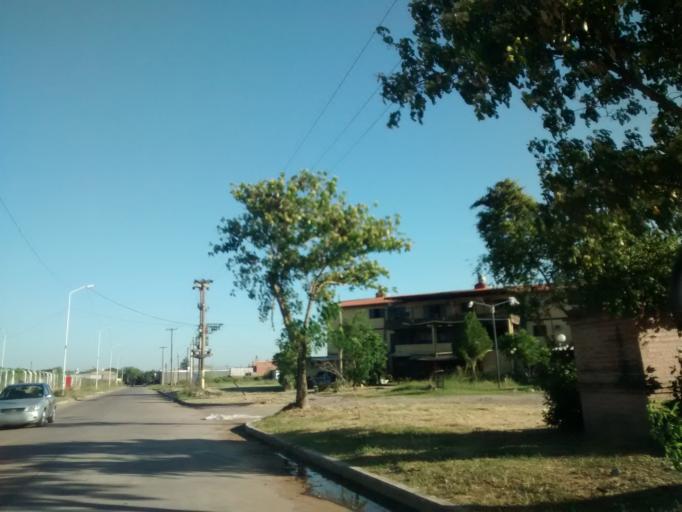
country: AR
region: Chaco
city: Fontana
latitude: -27.4449
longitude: -59.0129
